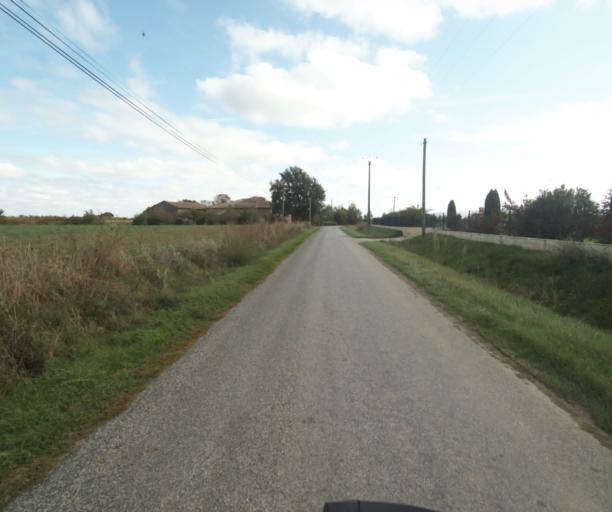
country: FR
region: Midi-Pyrenees
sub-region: Departement du Tarn-et-Garonne
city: Saint-Porquier
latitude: 43.9565
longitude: 1.1519
